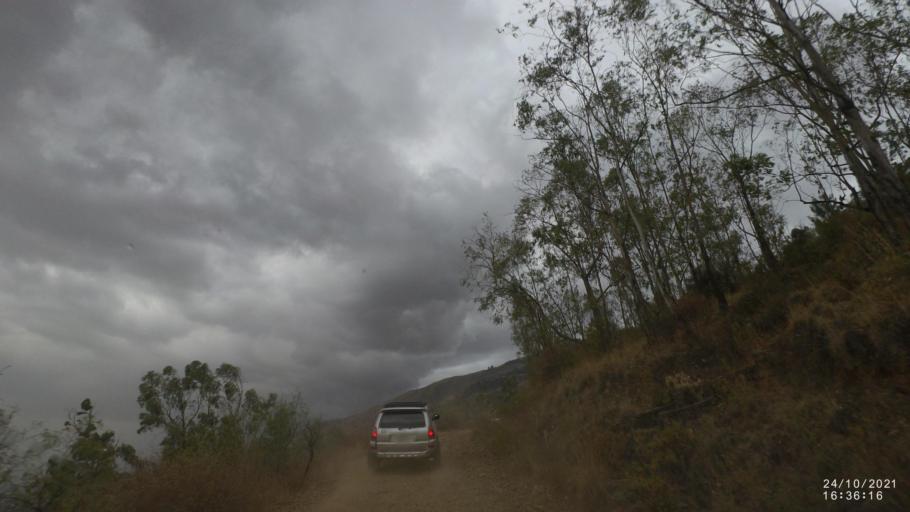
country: BO
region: Cochabamba
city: Cochabamba
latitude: -17.3446
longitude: -66.1490
